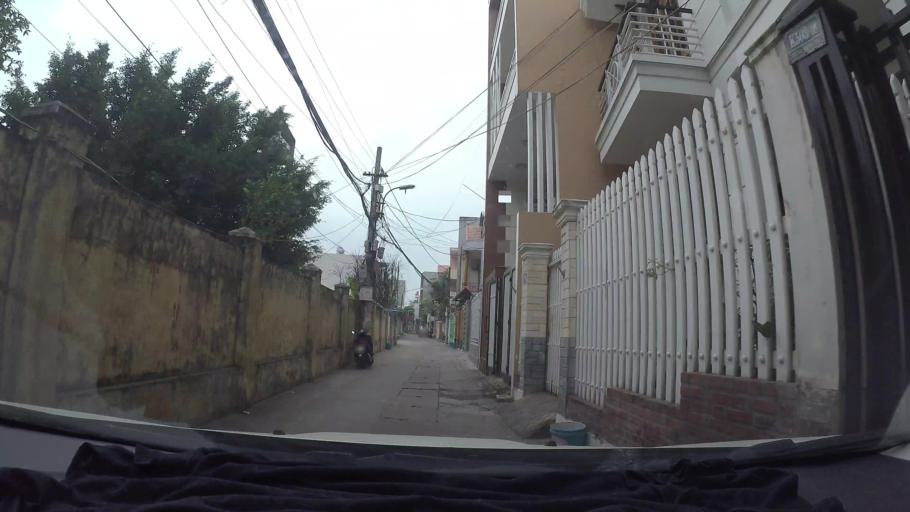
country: VN
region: Da Nang
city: Cam Le
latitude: 16.0416
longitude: 108.2065
